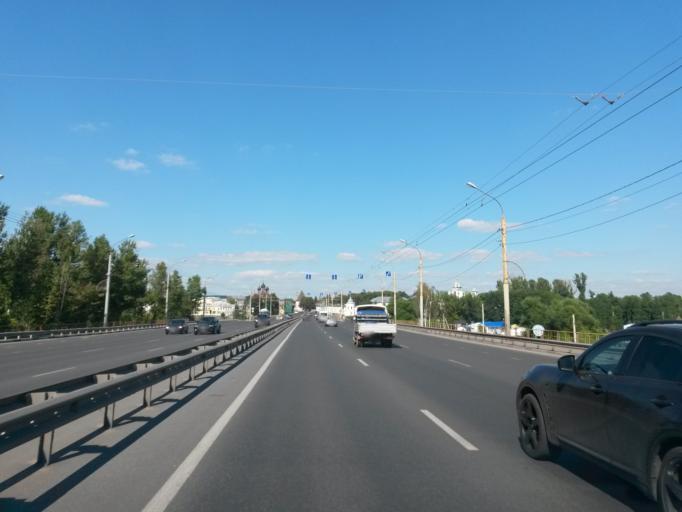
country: RU
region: Jaroslavl
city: Yaroslavl
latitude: 57.6163
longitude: 39.8847
